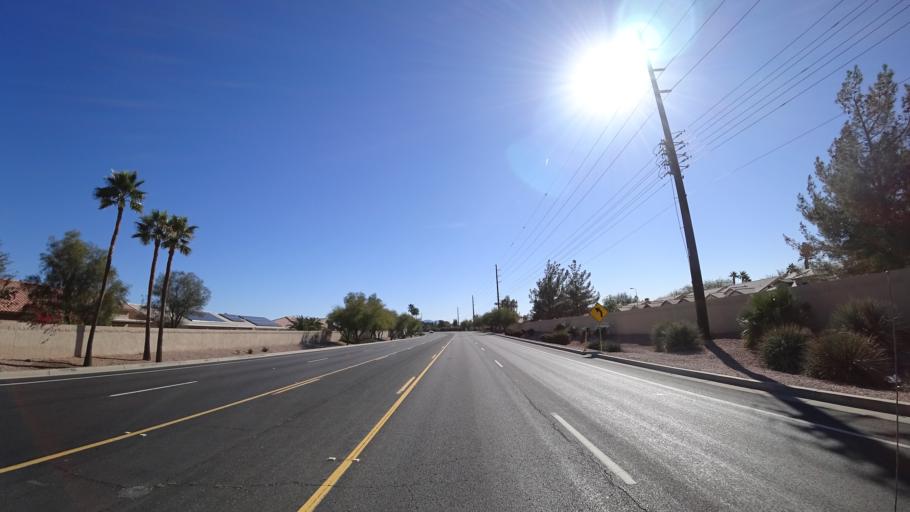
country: US
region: Arizona
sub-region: Maricopa County
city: Sun Lakes
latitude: 33.2188
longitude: -111.8897
